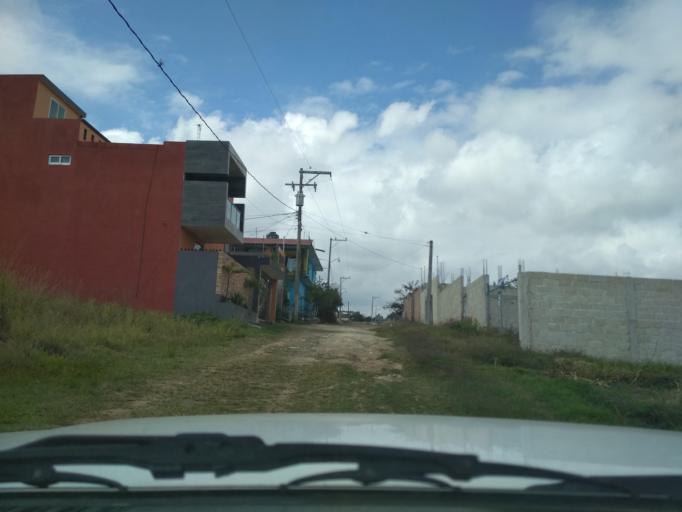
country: MX
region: Veracruz
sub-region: Emiliano Zapata
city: Jacarandas
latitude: 19.4961
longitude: -96.8390
